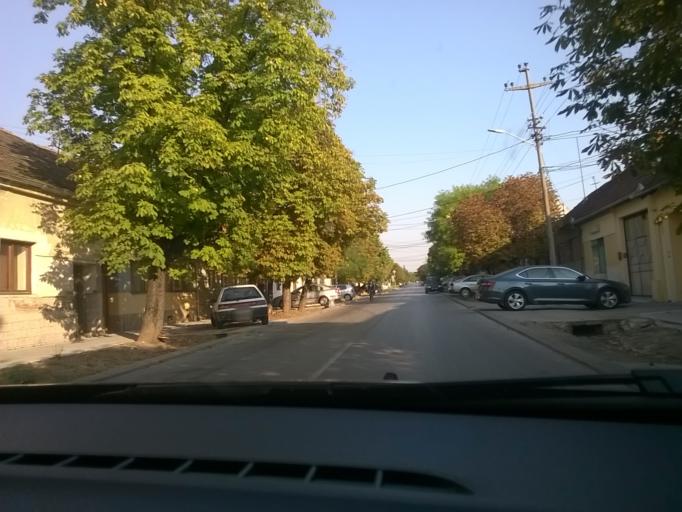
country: RS
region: Autonomna Pokrajina Vojvodina
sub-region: Juznobanatski Okrug
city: Vrsac
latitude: 45.1139
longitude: 21.3029
